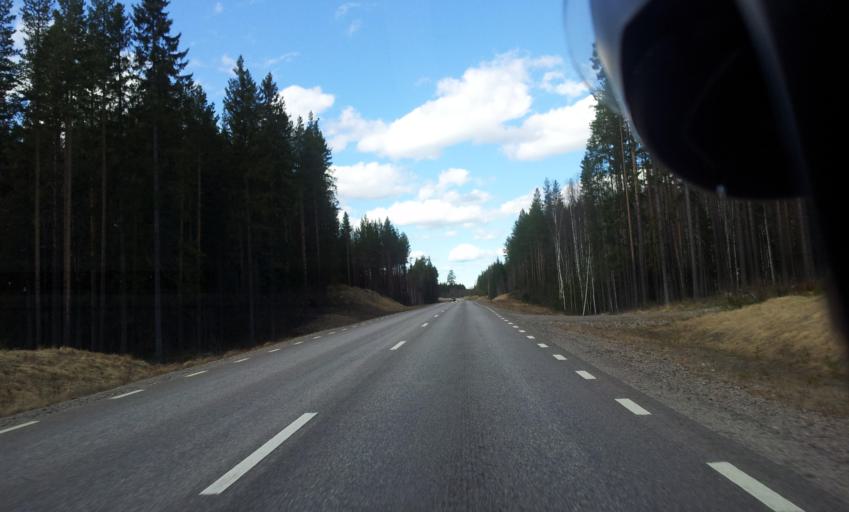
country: SE
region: Gaevleborg
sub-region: Ovanakers Kommun
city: Edsbyn
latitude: 61.1794
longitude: 15.8795
